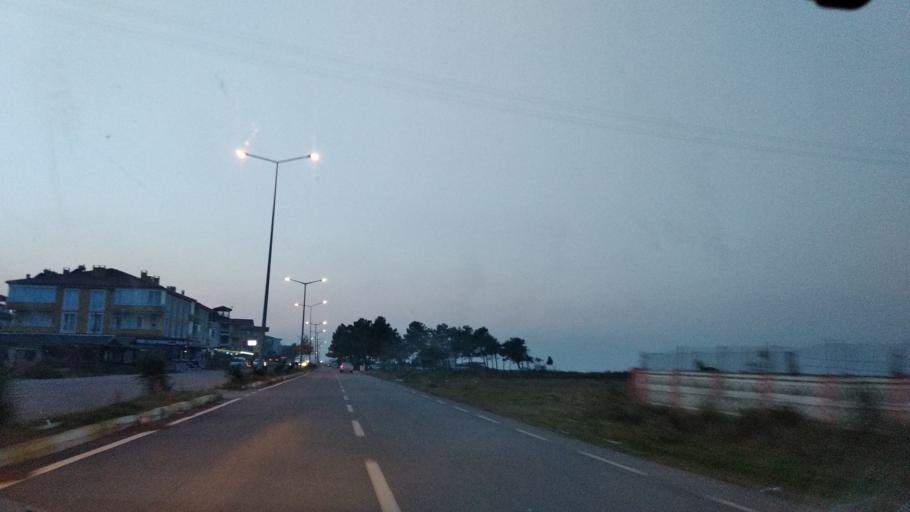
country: TR
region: Sakarya
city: Karasu
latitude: 41.0942
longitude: 30.7348
